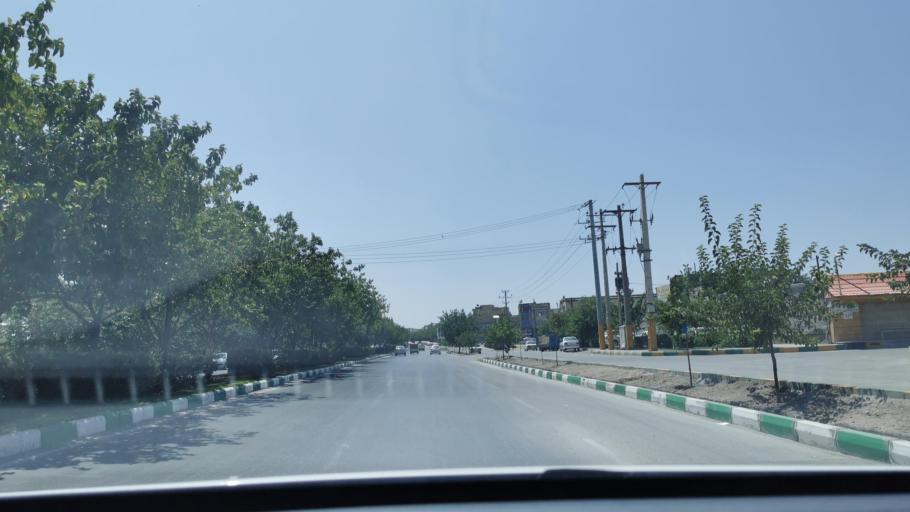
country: IR
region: Razavi Khorasan
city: Mashhad
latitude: 36.3499
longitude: 59.6290
